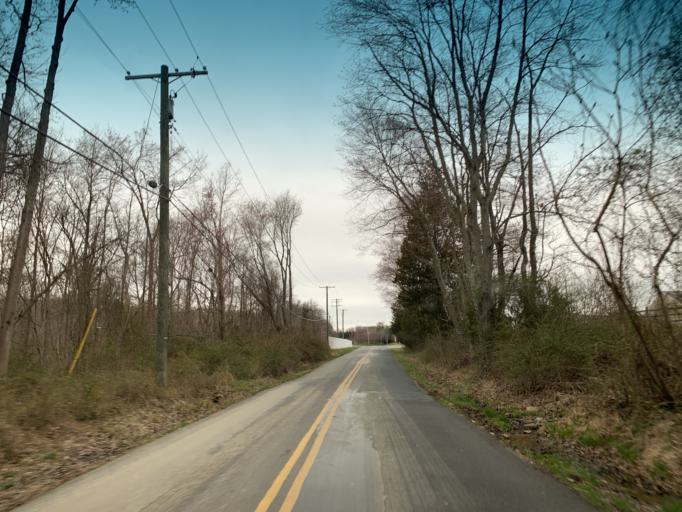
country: US
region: Maryland
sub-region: Harford County
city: Aberdeen
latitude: 39.5411
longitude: -76.1972
